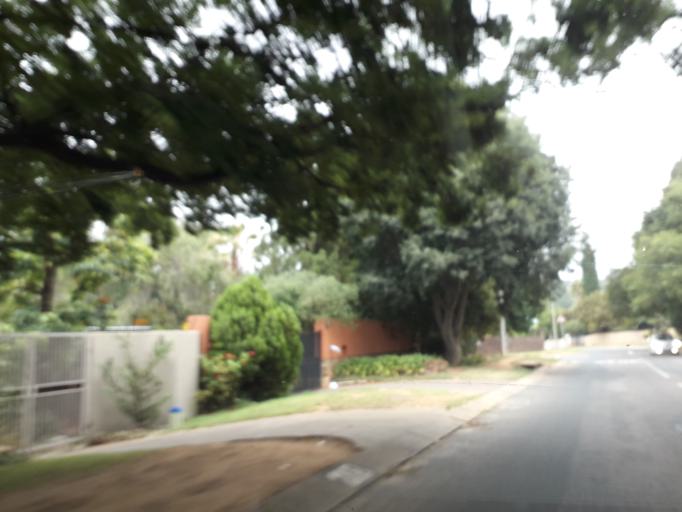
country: ZA
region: Gauteng
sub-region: City of Johannesburg Metropolitan Municipality
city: Roodepoort
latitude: -26.1101
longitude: 27.9393
